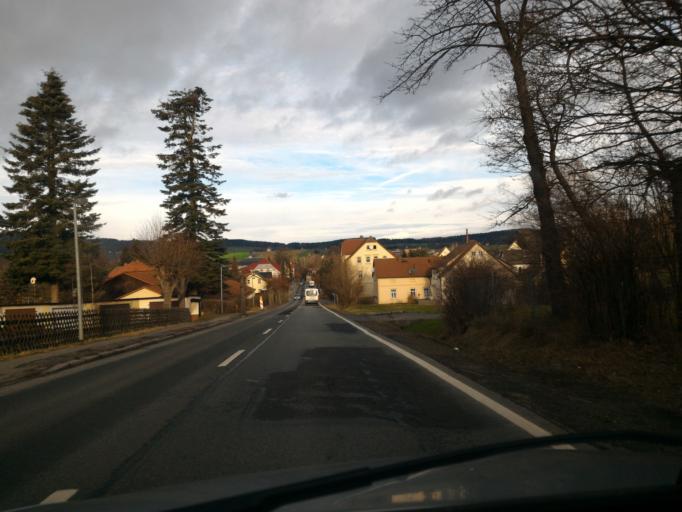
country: DE
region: Saxony
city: Oppach
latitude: 51.0545
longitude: 14.5062
